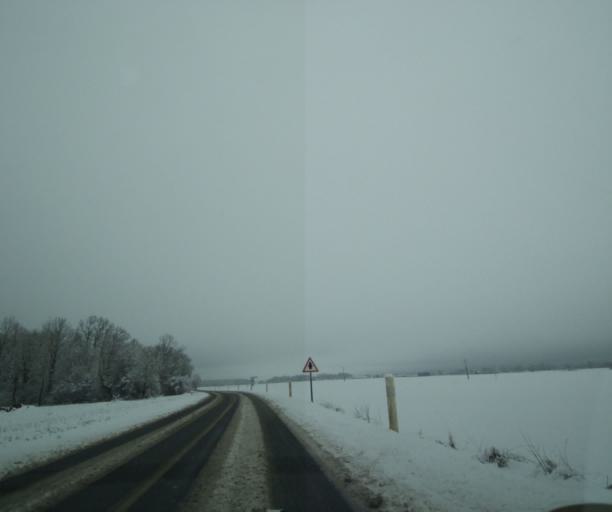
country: FR
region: Champagne-Ardenne
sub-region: Departement de la Haute-Marne
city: Wassy
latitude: 48.5621
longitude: 4.9226
